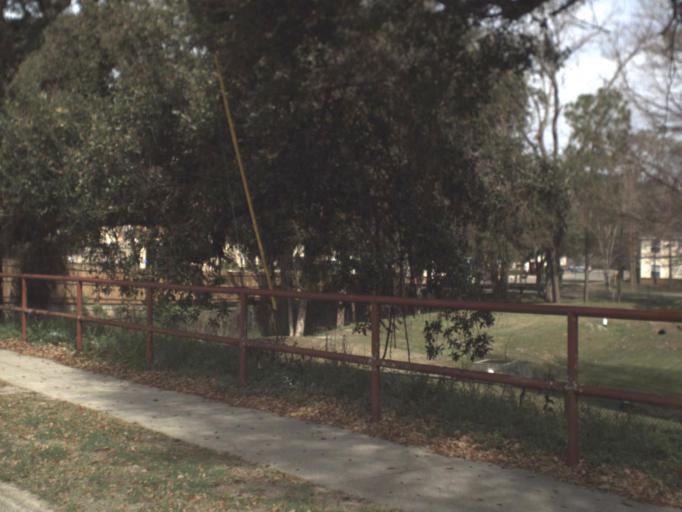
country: US
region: Florida
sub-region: Leon County
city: Tallahassee
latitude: 30.4482
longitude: -84.3021
